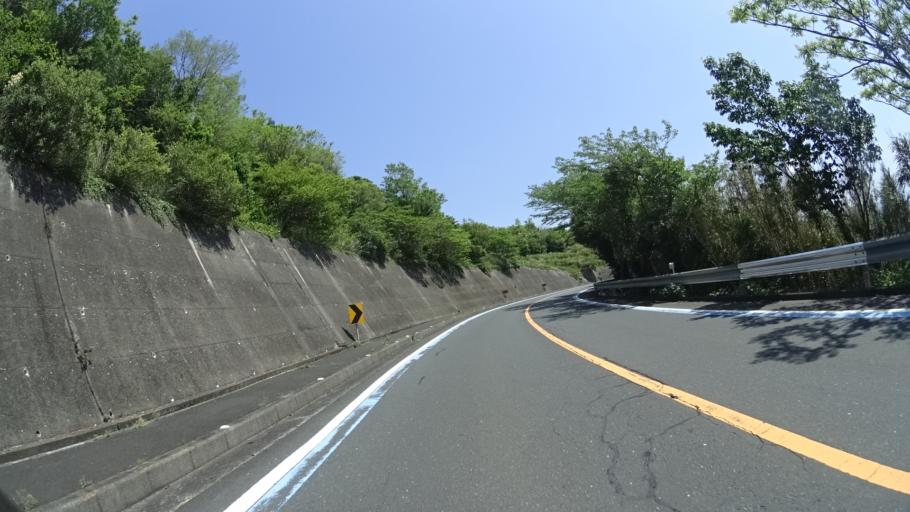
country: JP
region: Ehime
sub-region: Nishiuwa-gun
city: Ikata-cho
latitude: 33.4673
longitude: 132.2766
